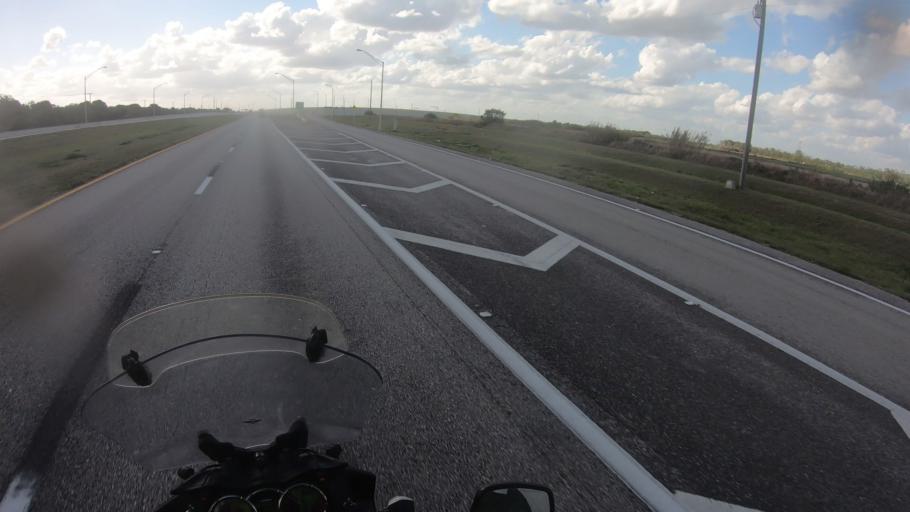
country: US
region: Florida
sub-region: Glades County
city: Moore Haven
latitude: 26.7533
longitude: -81.0747
